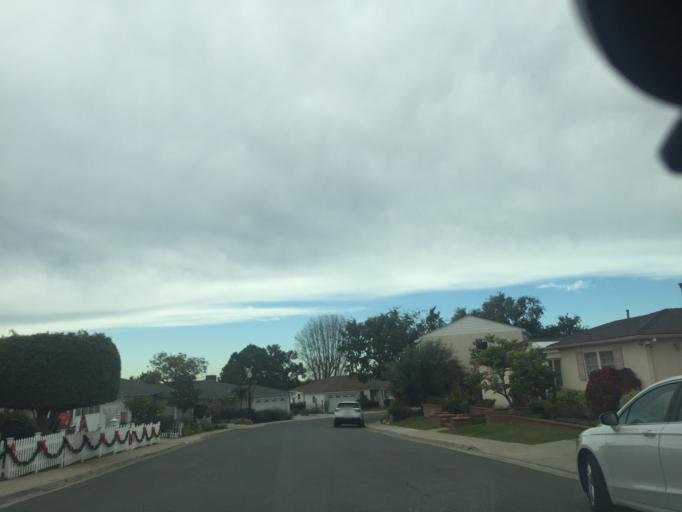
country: US
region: California
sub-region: San Diego County
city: Lemon Grove
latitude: 32.7661
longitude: -117.0909
